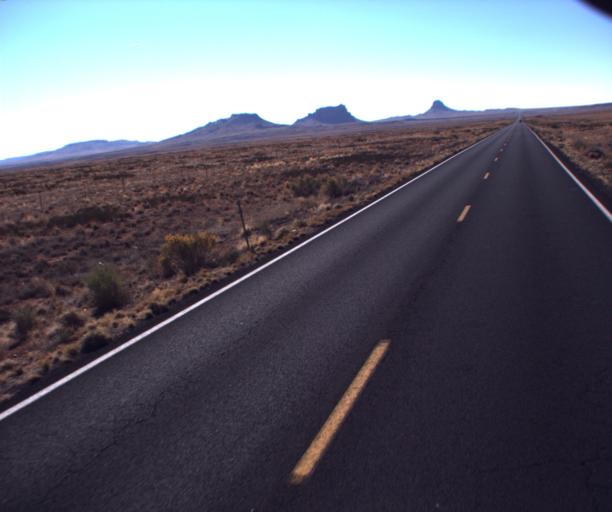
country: US
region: Arizona
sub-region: Navajo County
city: Dilkon
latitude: 35.3829
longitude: -110.4255
